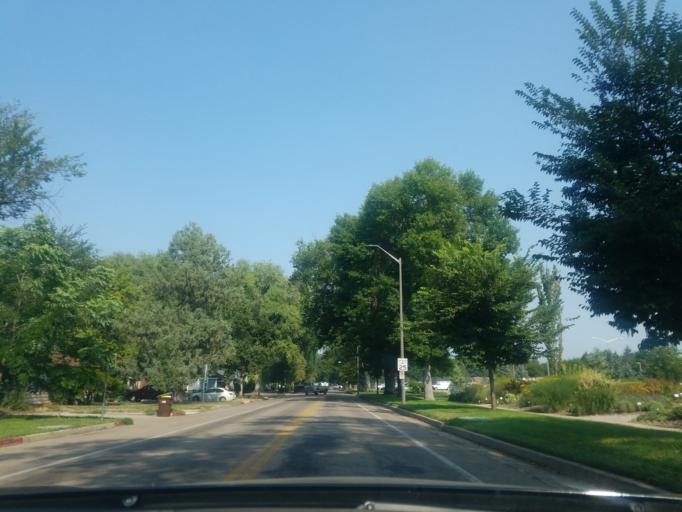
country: US
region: Colorado
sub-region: Larimer County
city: Fort Collins
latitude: 40.5710
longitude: -105.0752
